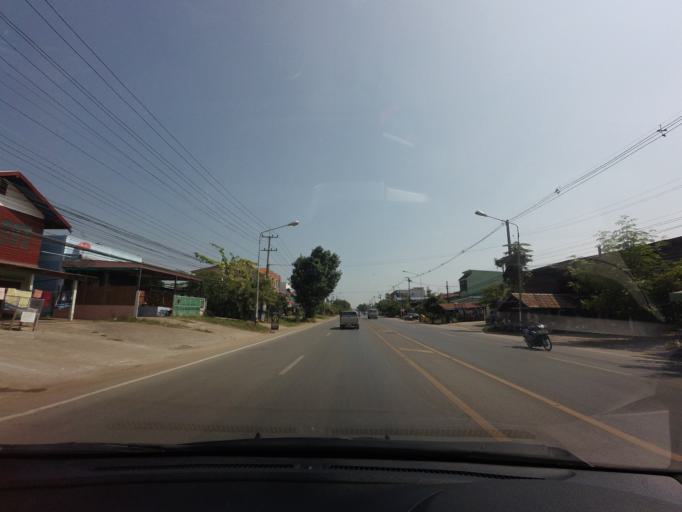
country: TH
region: Sukhothai
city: Sukhothai
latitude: 17.0109
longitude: 99.7853
